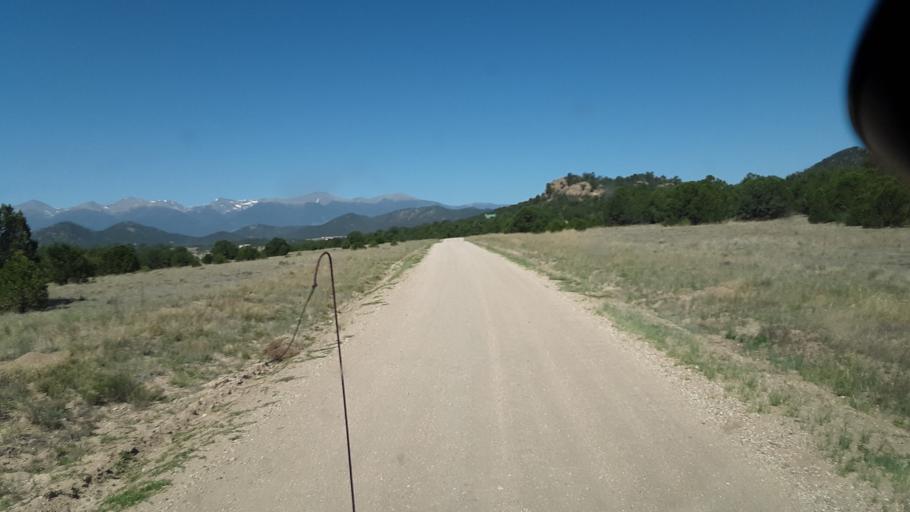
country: US
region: Colorado
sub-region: Custer County
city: Westcliffe
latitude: 38.2951
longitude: -105.4733
